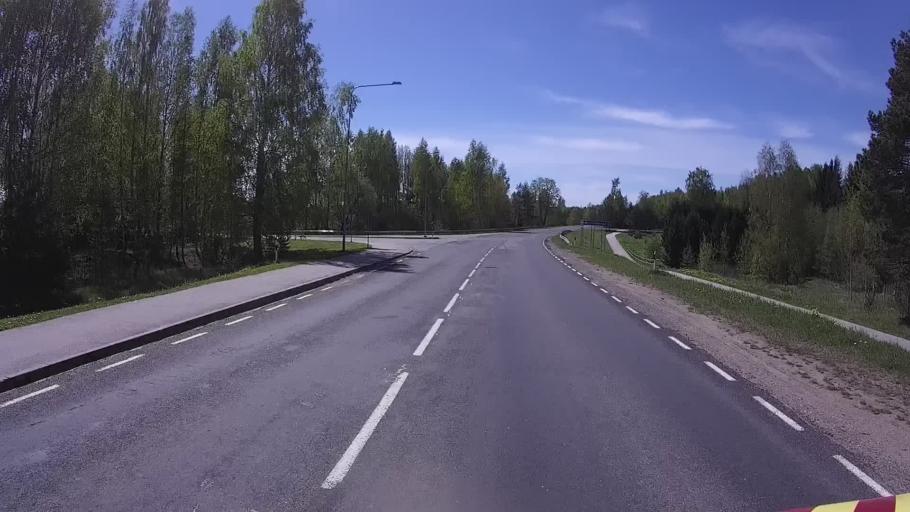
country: EE
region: Polvamaa
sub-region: Raepina vald
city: Rapina
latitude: 57.9944
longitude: 27.3347
